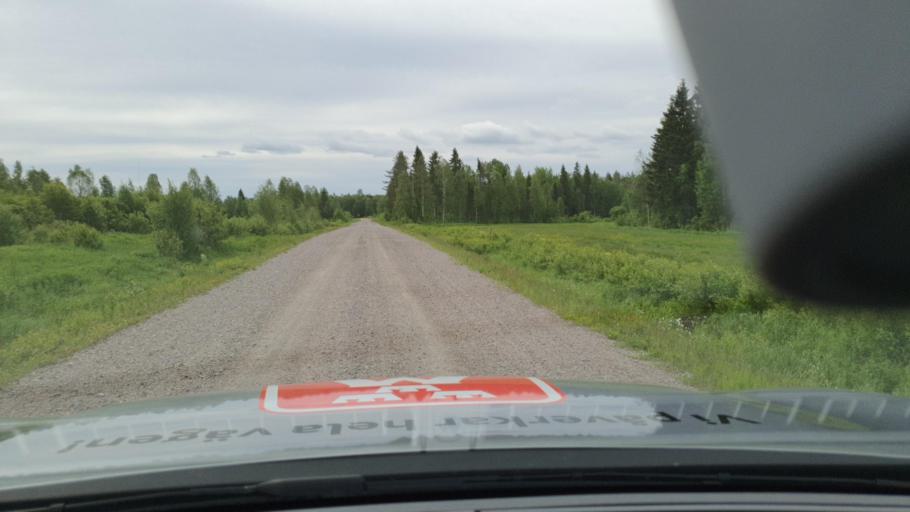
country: SE
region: Norrbotten
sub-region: Kalix Kommun
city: Kalix
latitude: 65.9842
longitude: 23.4591
